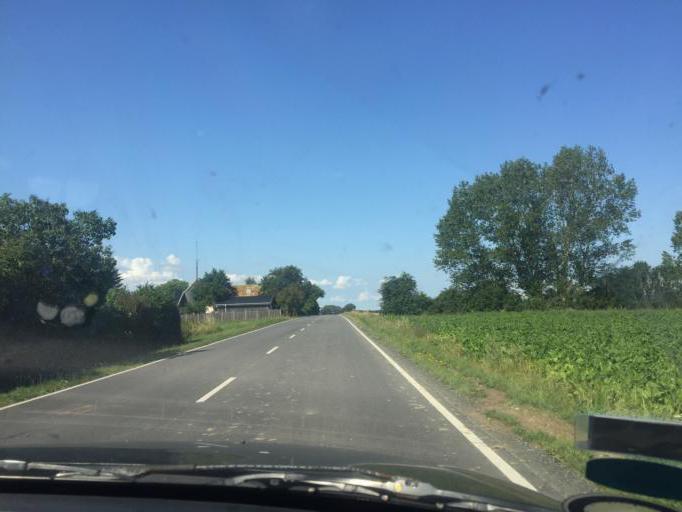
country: DK
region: Zealand
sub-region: Lolland Kommune
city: Maribo
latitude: 54.7966
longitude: 11.5556
